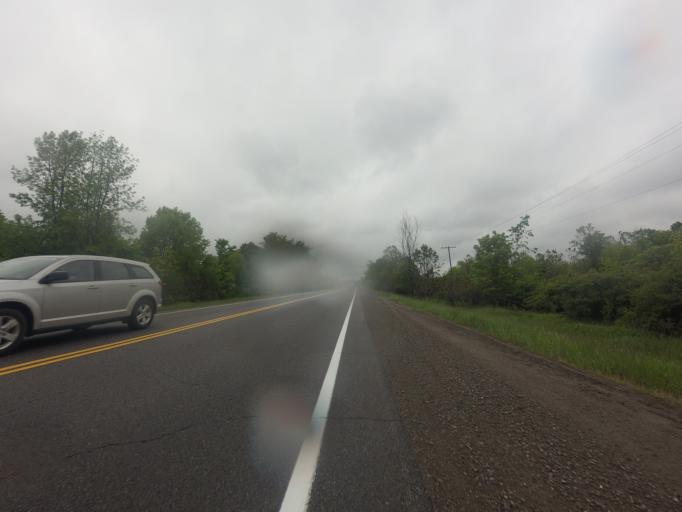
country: CA
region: Ontario
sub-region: Lanark County
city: Smiths Falls
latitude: 44.8480
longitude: -76.0577
